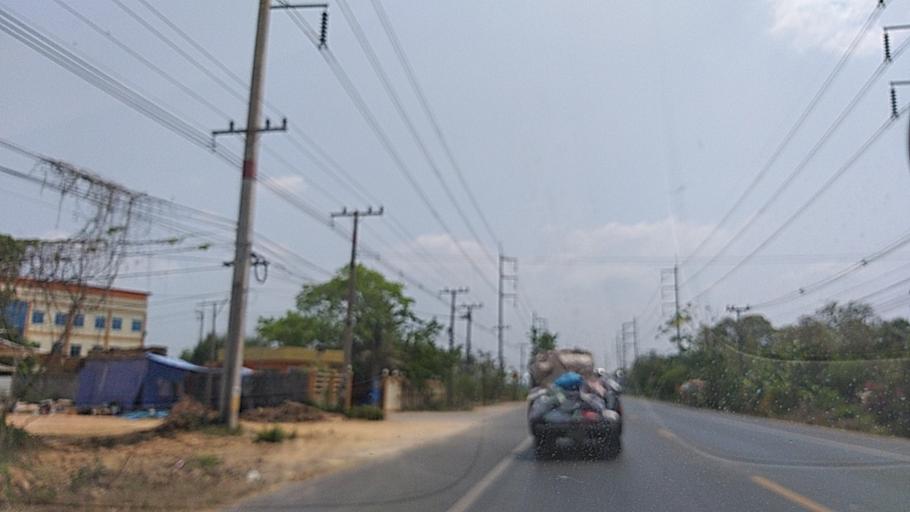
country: TH
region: Chachoengsao
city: Bang Nam Priao
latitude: 13.7814
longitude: 101.0606
